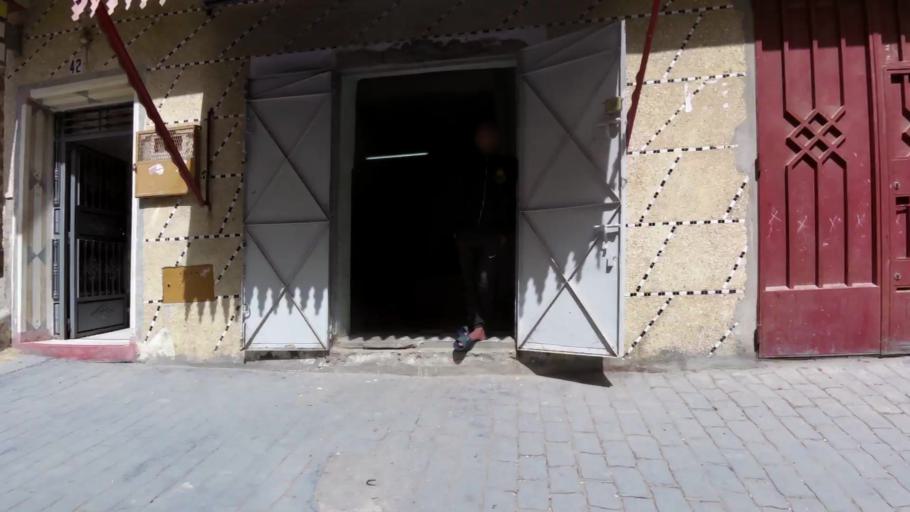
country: MA
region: Tanger-Tetouan
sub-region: Tanger-Assilah
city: Tangier
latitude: 35.7460
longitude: -5.8322
